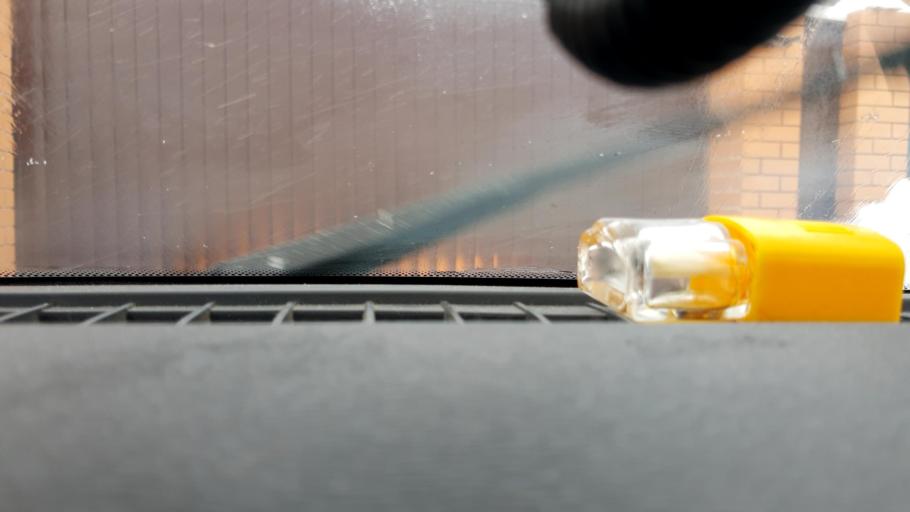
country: RU
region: Bashkortostan
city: Kabakovo
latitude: 54.6167
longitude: 56.1146
